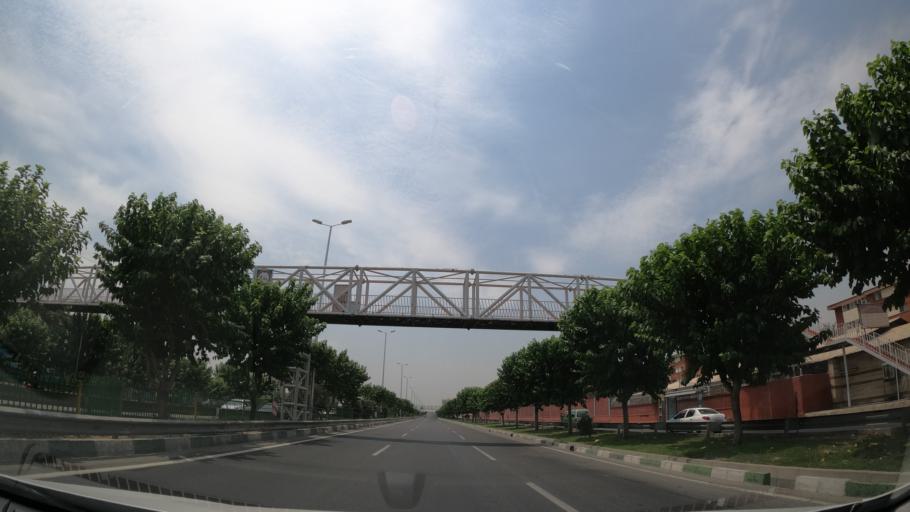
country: IR
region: Tehran
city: Tehran
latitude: 35.6753
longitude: 51.3172
